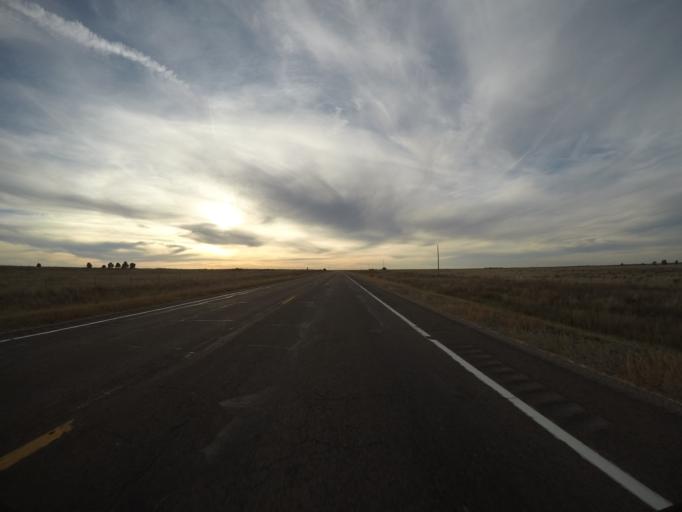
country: US
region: Colorado
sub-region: Yuma County
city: Yuma
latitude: 39.6702
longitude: -102.8893
